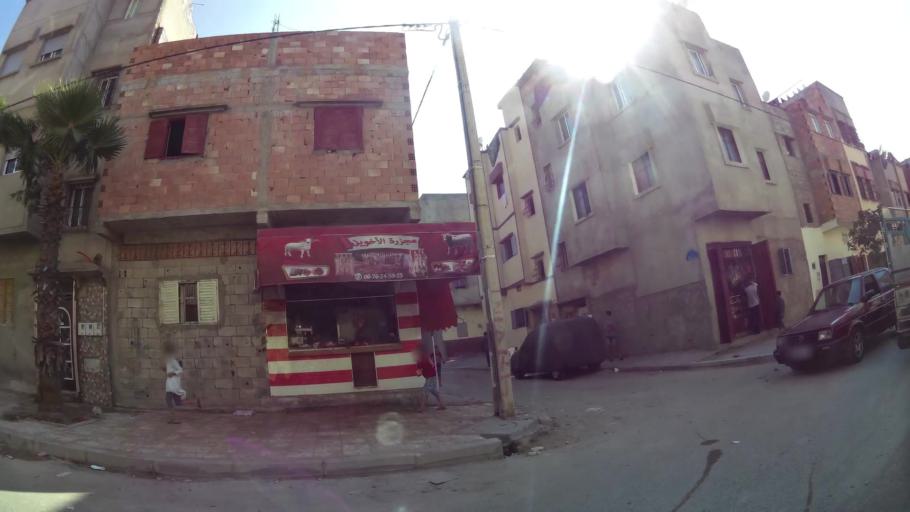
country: MA
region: Rabat-Sale-Zemmour-Zaer
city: Sale
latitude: 34.0565
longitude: -6.7724
